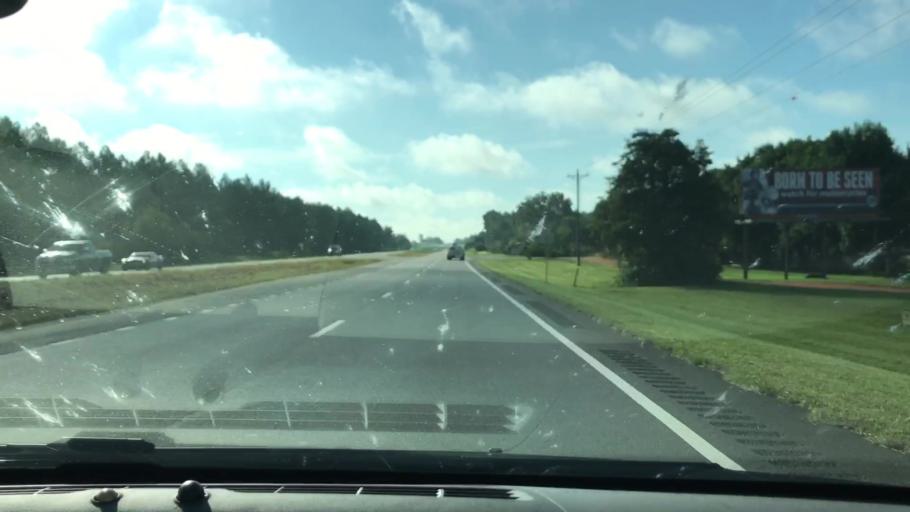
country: US
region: Georgia
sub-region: Terrell County
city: Dawson
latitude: 31.7436
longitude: -84.4152
